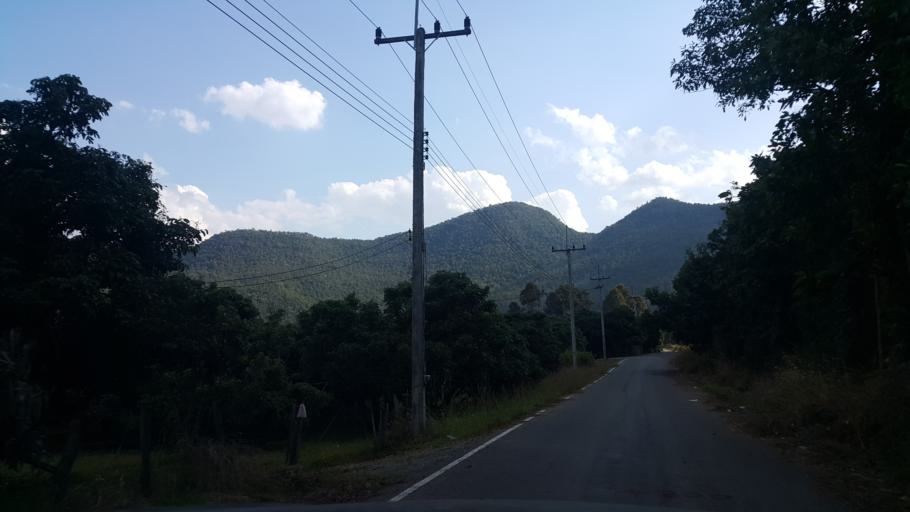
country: TH
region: Lamphun
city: Ban Thi
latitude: 18.5890
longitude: 99.1316
